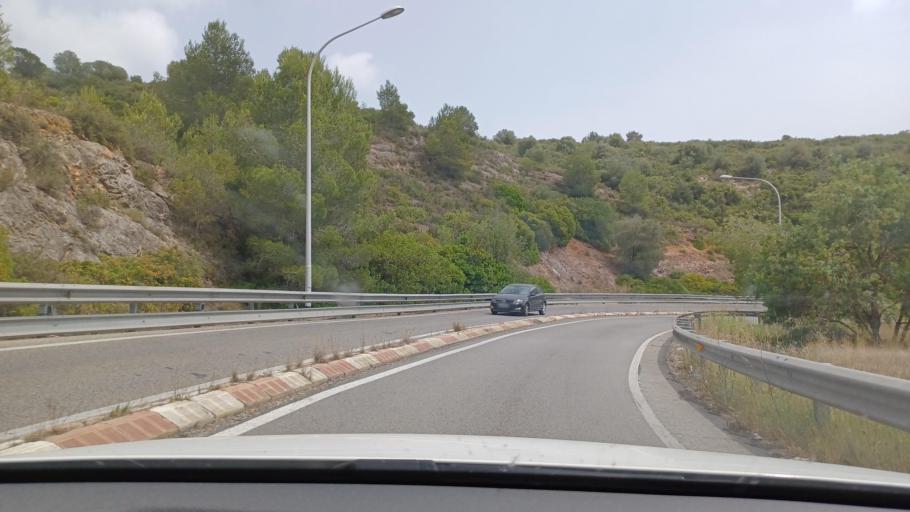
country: ES
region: Catalonia
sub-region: Provincia de Tarragona
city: Tarragona
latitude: 41.1409
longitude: 1.2395
